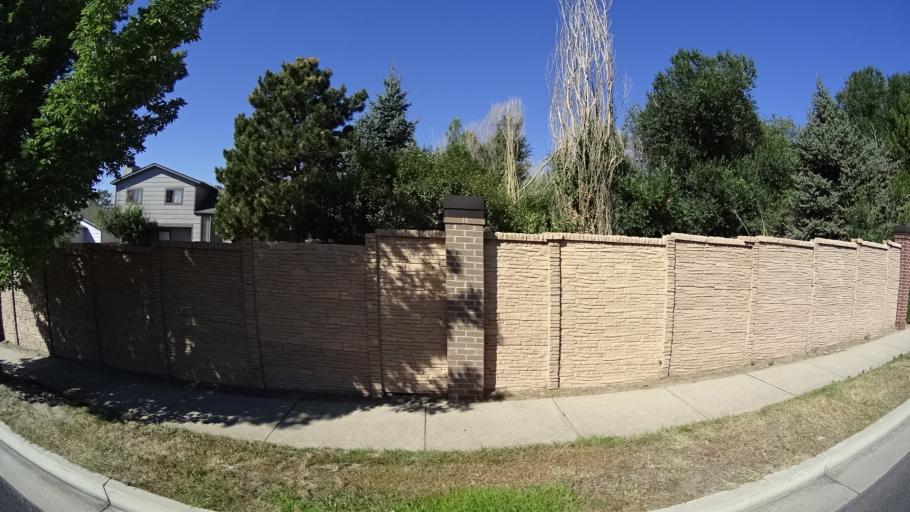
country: US
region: Colorado
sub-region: El Paso County
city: Black Forest
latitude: 38.9353
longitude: -104.7555
